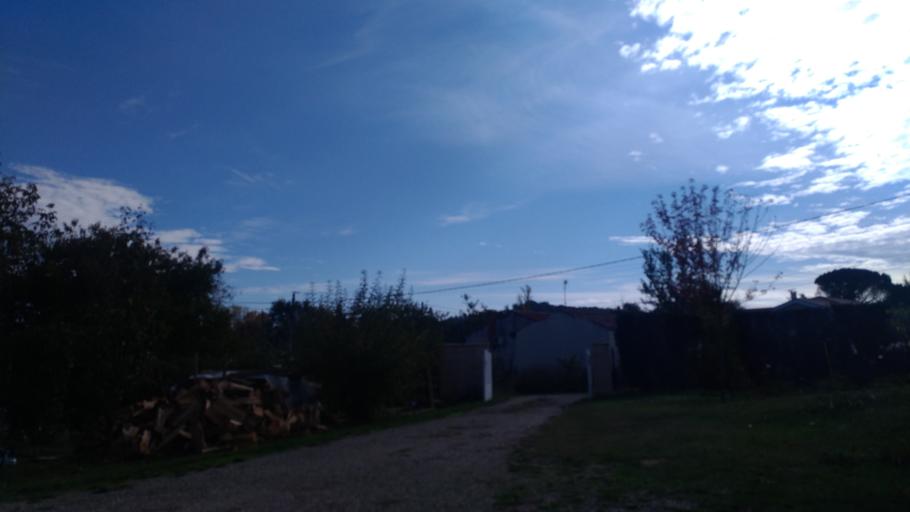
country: FR
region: Midi-Pyrenees
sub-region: Departement du Tarn
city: Puygouzon
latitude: 43.9169
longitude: 2.1791
